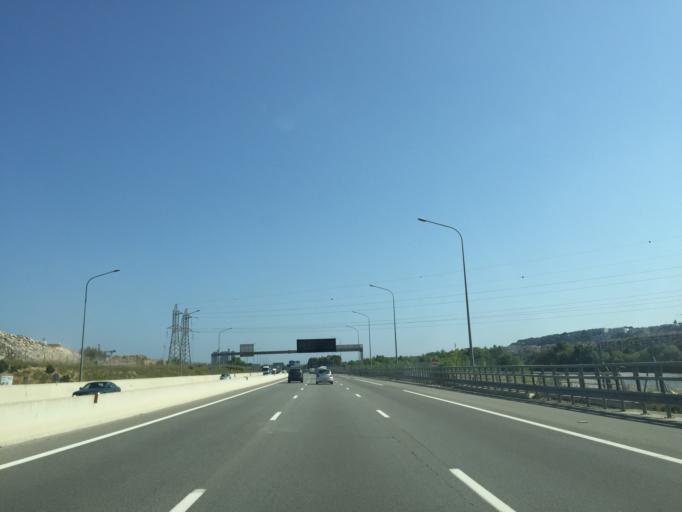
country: FR
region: Provence-Alpes-Cote d'Azur
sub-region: Departement des Alpes-Maritimes
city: Saint-Laurent-du-Var
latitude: 43.6876
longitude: 7.1905
